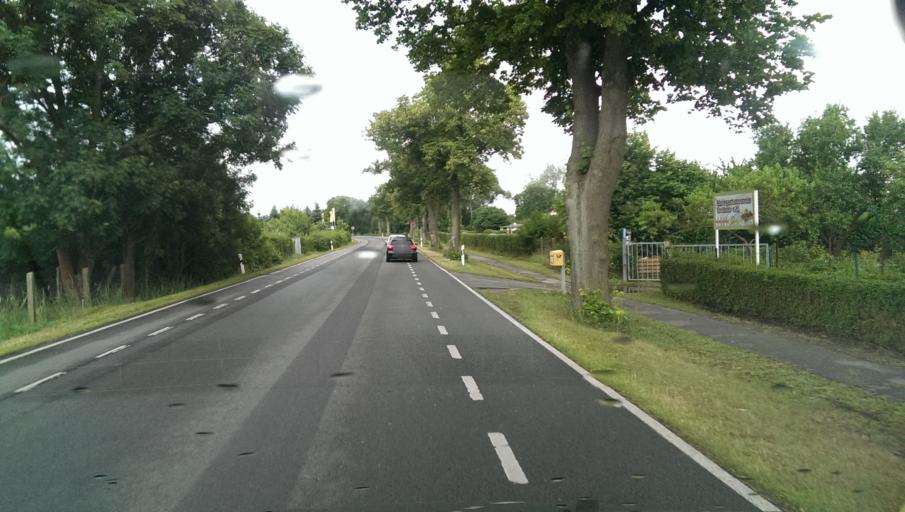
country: DE
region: Brandenburg
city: Rathenow
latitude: 52.6215
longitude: 12.3310
